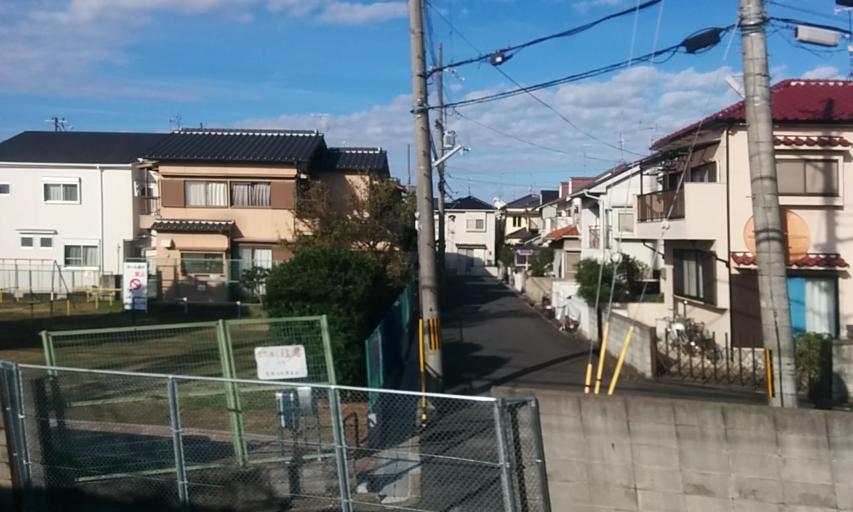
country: JP
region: Kyoto
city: Tanabe
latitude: 34.8592
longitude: 135.7735
